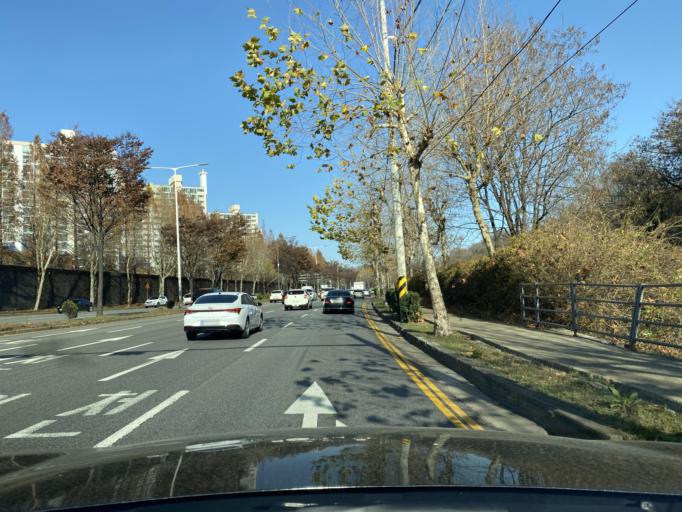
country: KR
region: Incheon
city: Incheon
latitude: 37.4396
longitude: 126.7405
